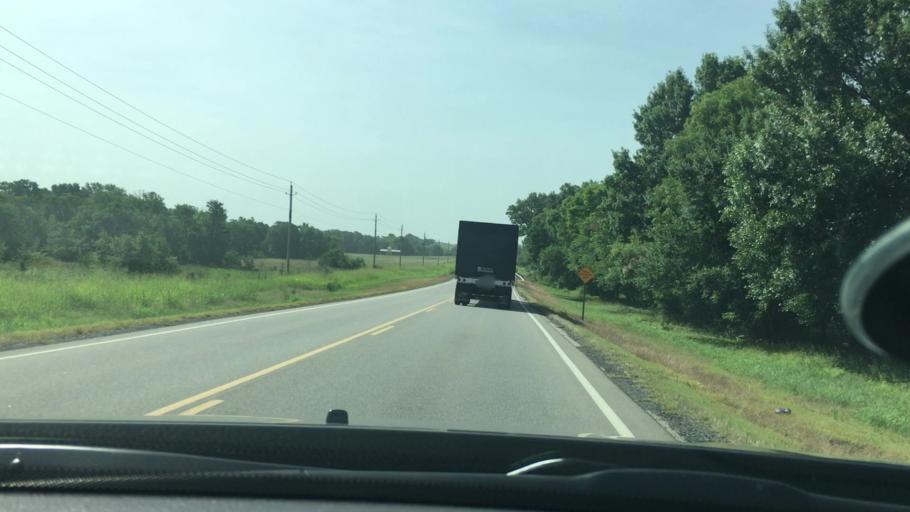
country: US
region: Oklahoma
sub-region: Atoka County
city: Atoka
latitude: 34.4128
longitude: -96.1845
